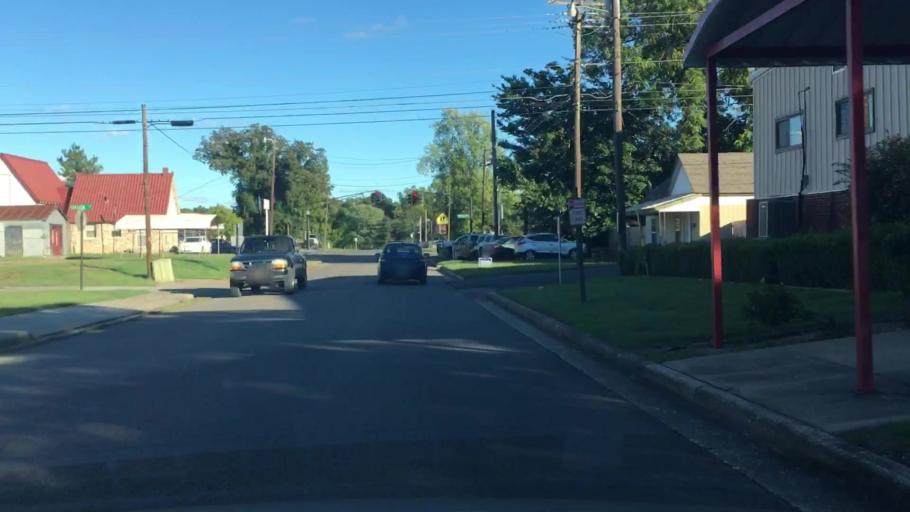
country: US
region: Oklahoma
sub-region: Cherokee County
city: Tahlequah
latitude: 35.9103
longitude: -94.9735
